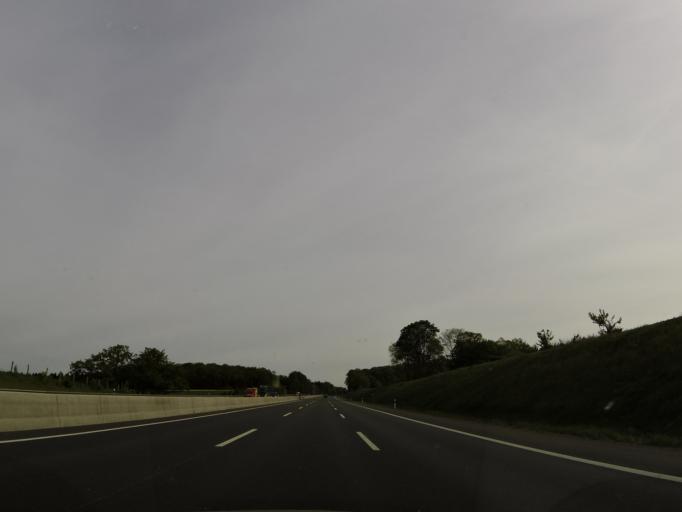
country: DE
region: Lower Saxony
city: Haverlah
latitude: 52.0282
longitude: 10.1718
